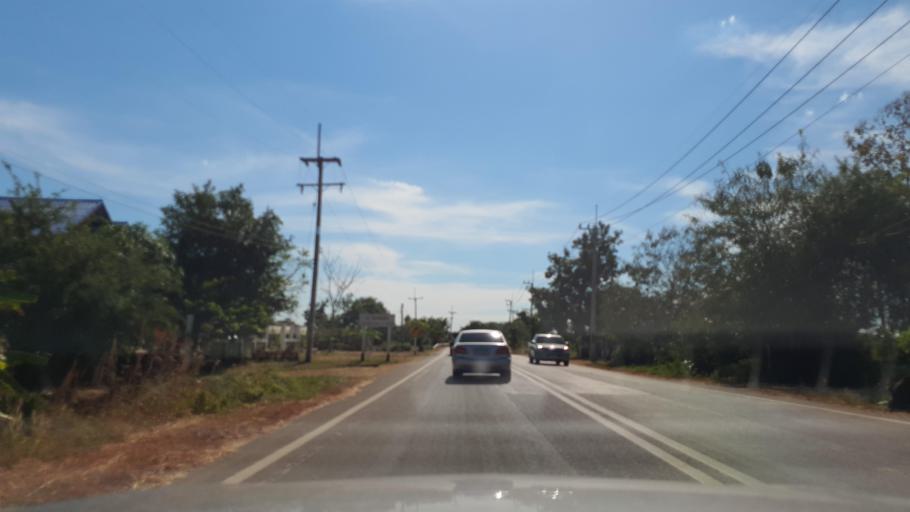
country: TH
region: Kalasin
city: Khao Wong
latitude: 16.7409
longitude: 104.1069
